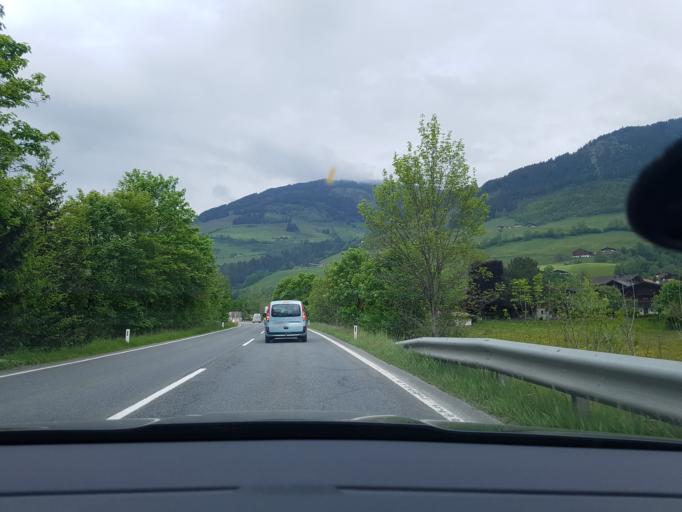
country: AT
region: Salzburg
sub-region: Politischer Bezirk Zell am See
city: Uttendorf
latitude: 47.2861
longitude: 12.5443
